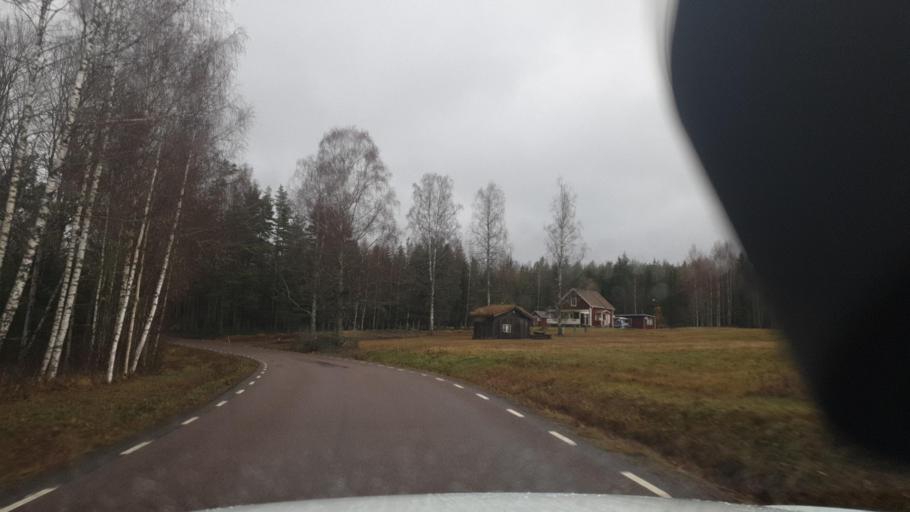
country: SE
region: Vaermland
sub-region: Eda Kommun
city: Charlottenberg
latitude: 59.7807
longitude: 12.2137
